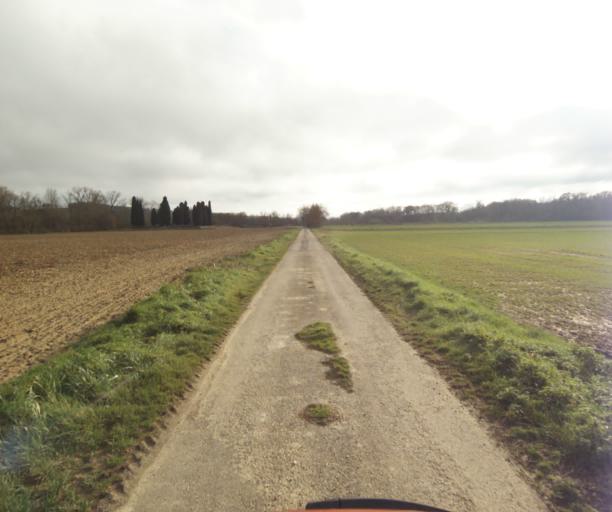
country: FR
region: Languedoc-Roussillon
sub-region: Departement de l'Aude
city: Belpech
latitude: 43.1873
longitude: 1.7335
